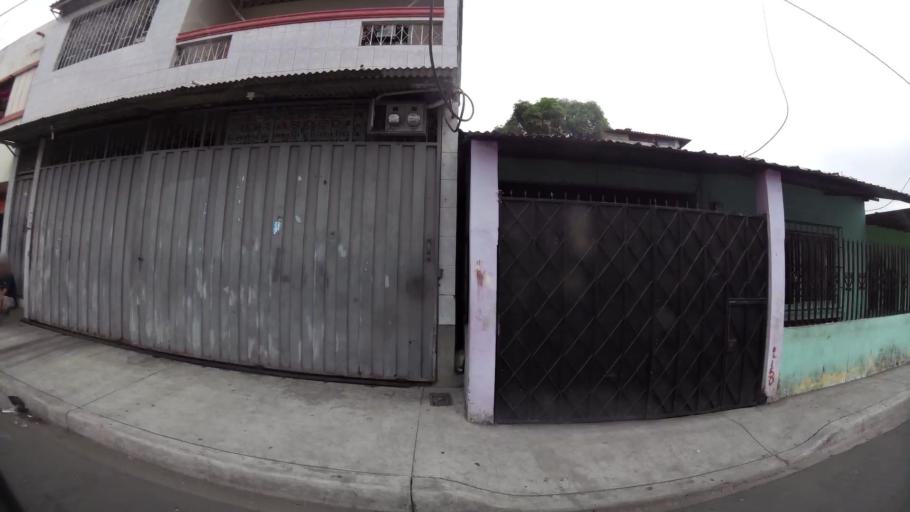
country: EC
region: Guayas
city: Guayaquil
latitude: -2.2374
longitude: -79.9066
